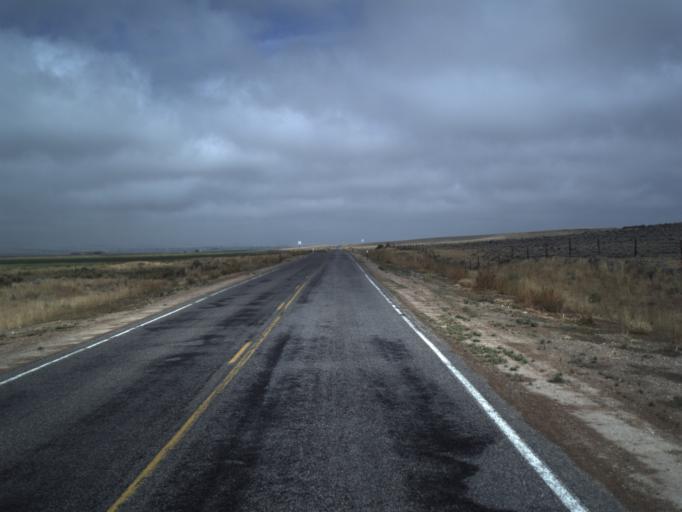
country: US
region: Utah
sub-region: Rich County
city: Randolph
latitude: 41.4663
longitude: -111.1037
